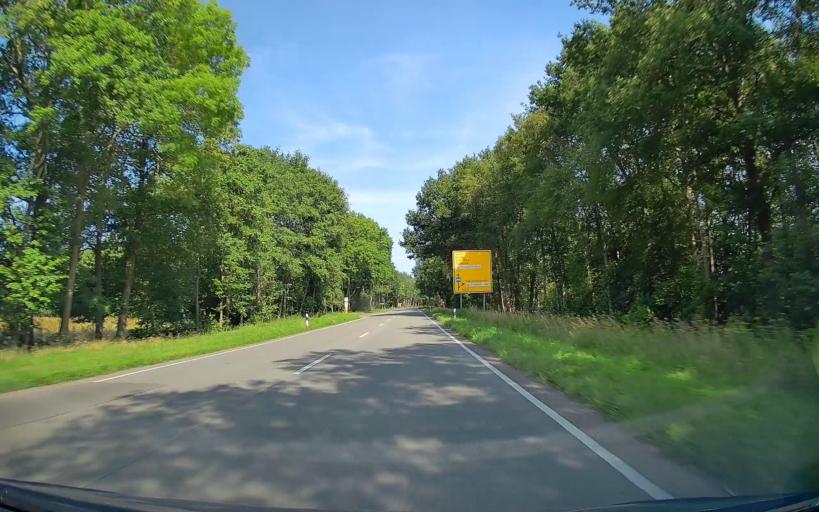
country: DE
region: Lower Saxony
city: Friesoythe
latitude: 53.0019
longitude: 7.8695
